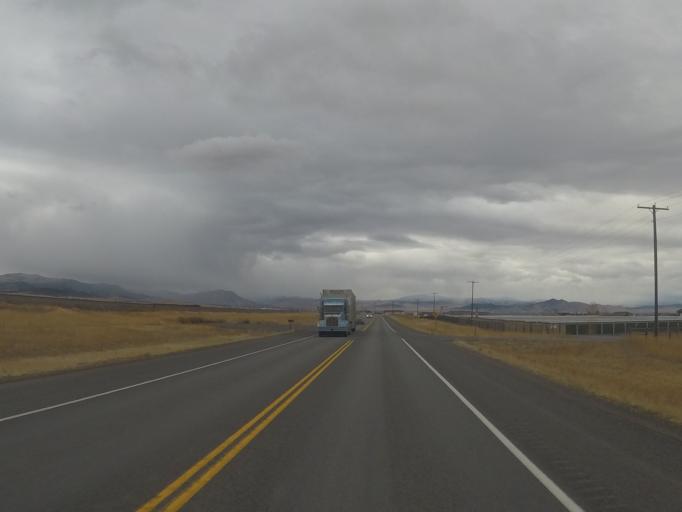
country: US
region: Montana
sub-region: Lewis and Clark County
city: East Helena
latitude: 46.5869
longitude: -111.8741
